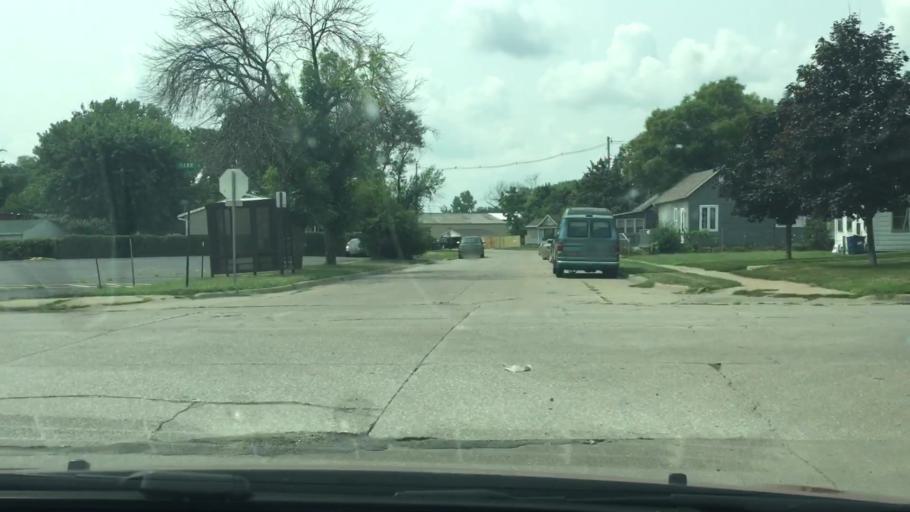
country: US
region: Iowa
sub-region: Muscatine County
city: Muscatine
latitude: 41.4095
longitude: -91.0646
